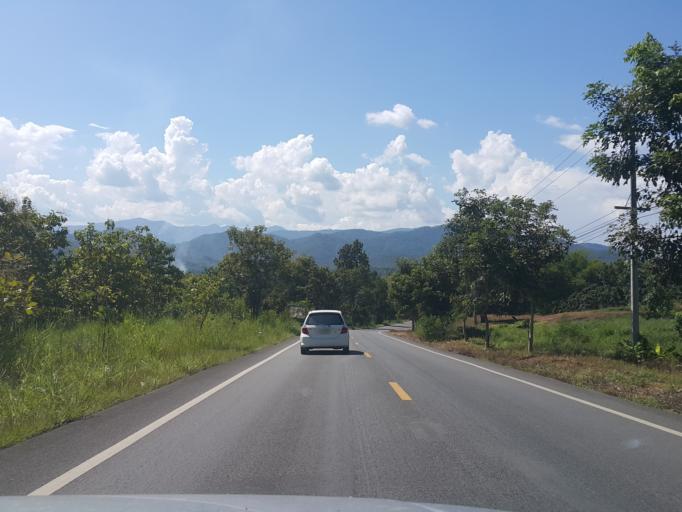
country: TH
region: Chiang Mai
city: Mae Taeng
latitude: 19.1638
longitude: 98.9358
